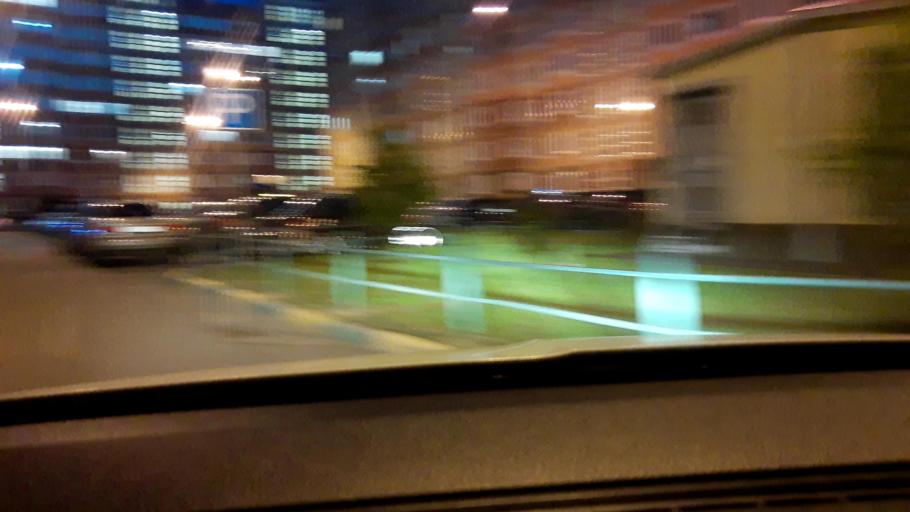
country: RU
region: Moscow
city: Zagor'ye
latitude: 55.5329
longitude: 37.6400
